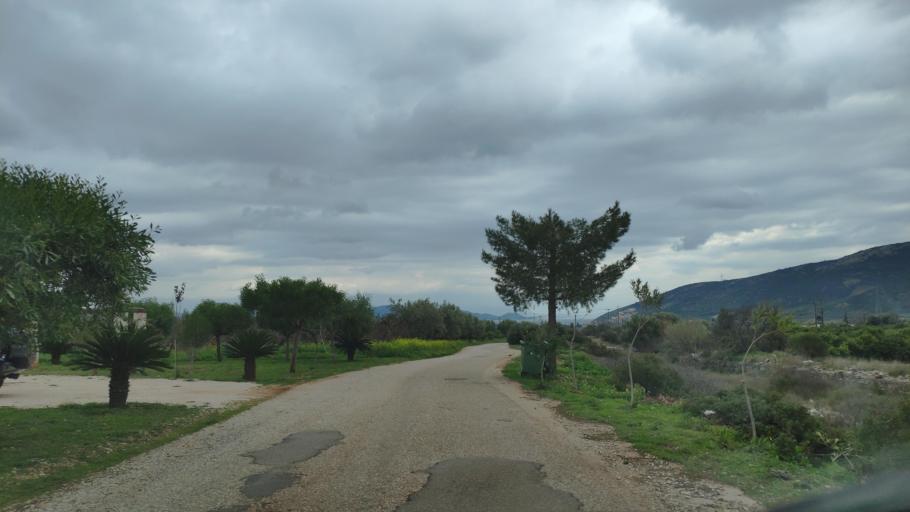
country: GR
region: Peloponnese
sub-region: Nomos Argolidos
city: Nea Kios
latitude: 37.5316
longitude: 22.6998
